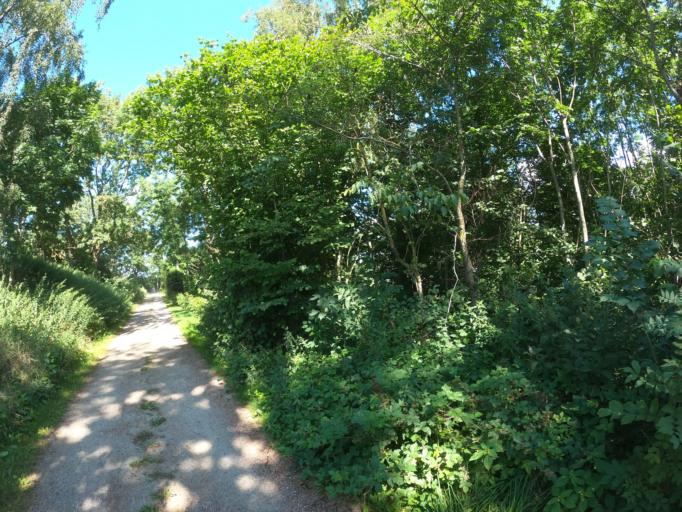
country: SE
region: Skane
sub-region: Lunds Kommun
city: Genarp
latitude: 55.6832
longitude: 13.3927
